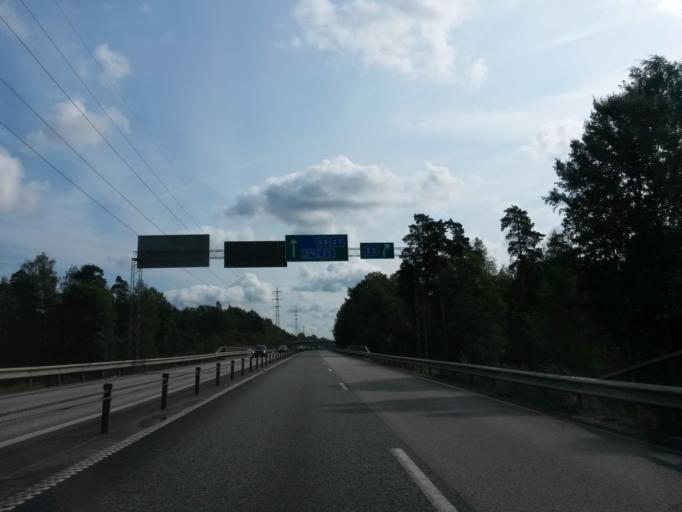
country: SE
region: Kronoberg
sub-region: Vaxjo Kommun
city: Vaexjoe
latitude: 56.9010
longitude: 14.7974
